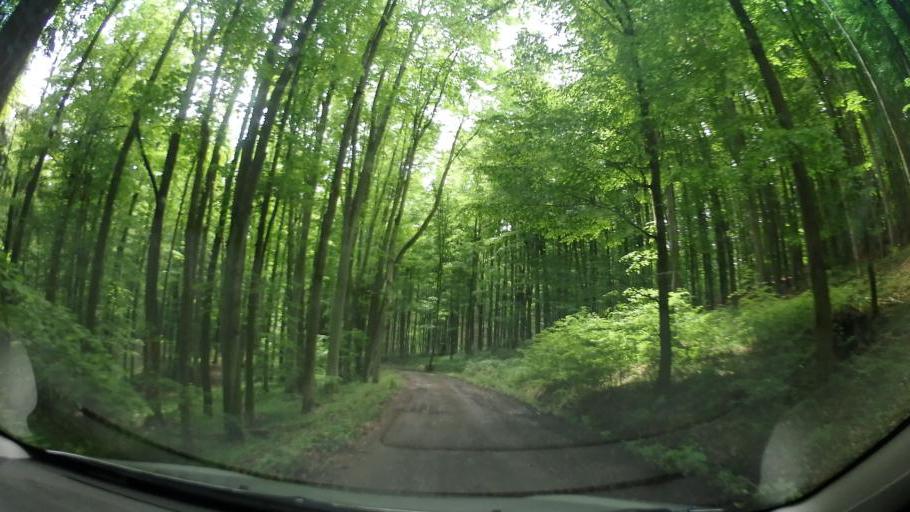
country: CZ
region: Olomoucky
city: Stity
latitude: 49.8712
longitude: 16.7378
